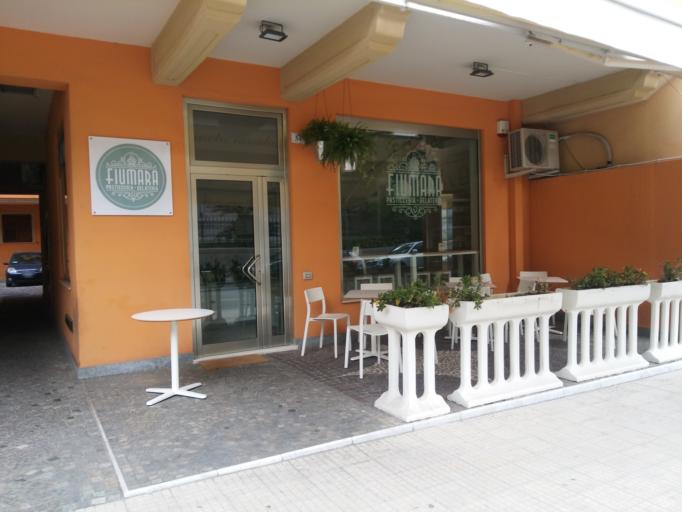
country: IT
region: Sicily
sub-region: Messina
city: Milazzo
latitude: 38.2212
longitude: 15.2392
